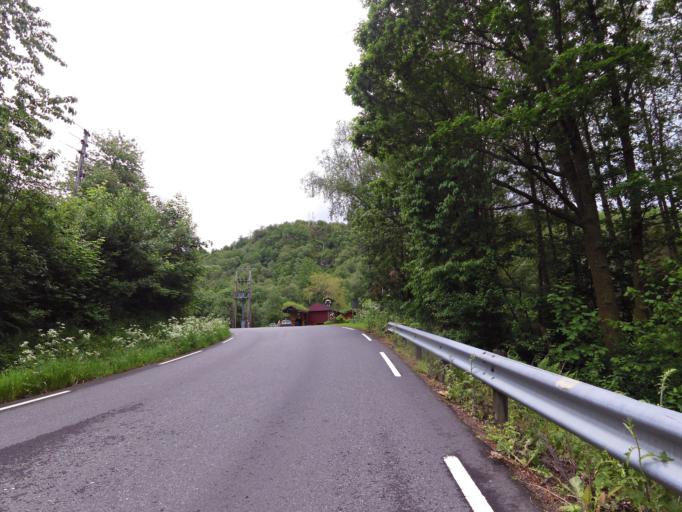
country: NO
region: Vest-Agder
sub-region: Lyngdal
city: Lyngdal
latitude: 58.1113
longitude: 6.9557
